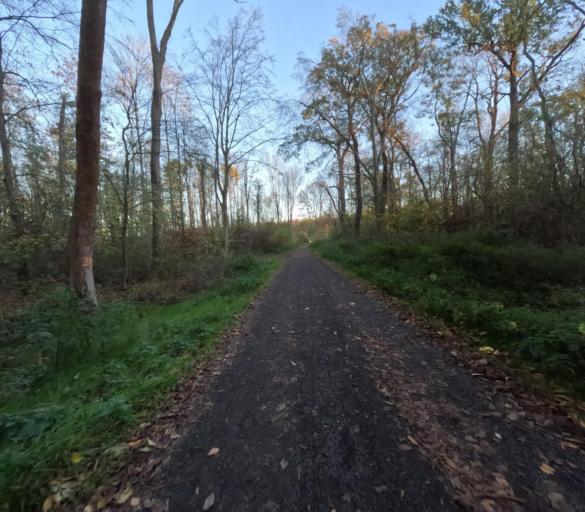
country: DE
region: Saxony
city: Schkeuditz
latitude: 51.3752
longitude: 12.2405
